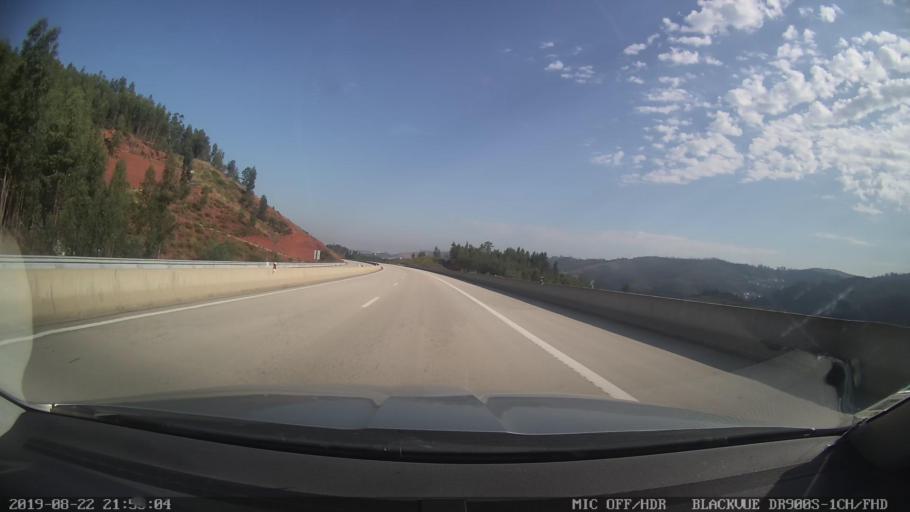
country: PT
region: Coimbra
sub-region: Coimbra
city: Coimbra
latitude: 40.1469
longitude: -8.3830
